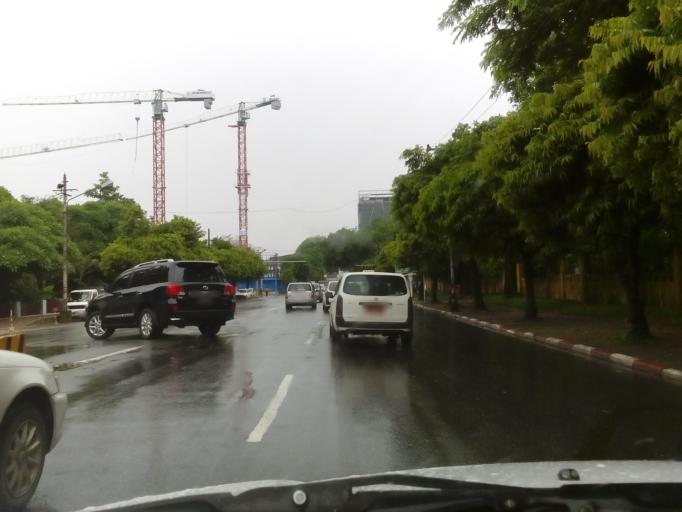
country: MM
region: Yangon
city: Yangon
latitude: 16.7806
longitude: 96.1533
